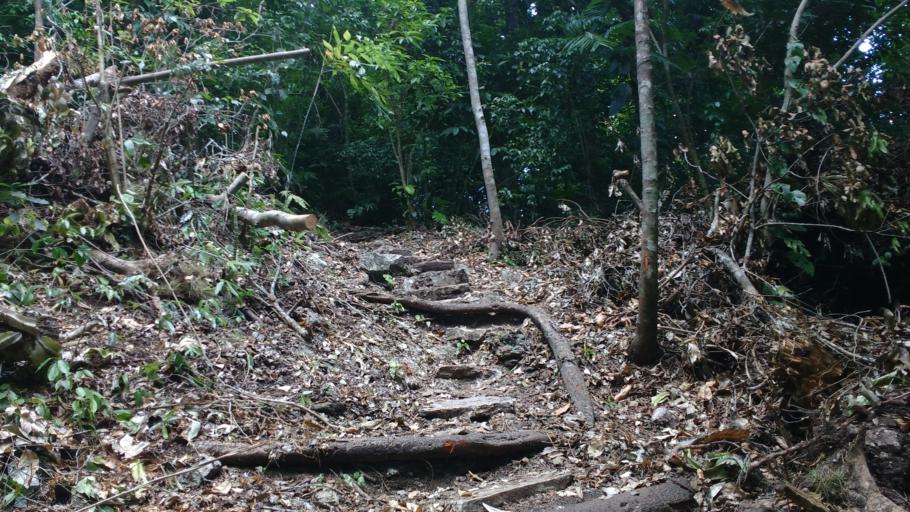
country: MX
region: Chiapas
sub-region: Ocosingo
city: Frontera Corozal
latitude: 16.9006
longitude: -90.9673
